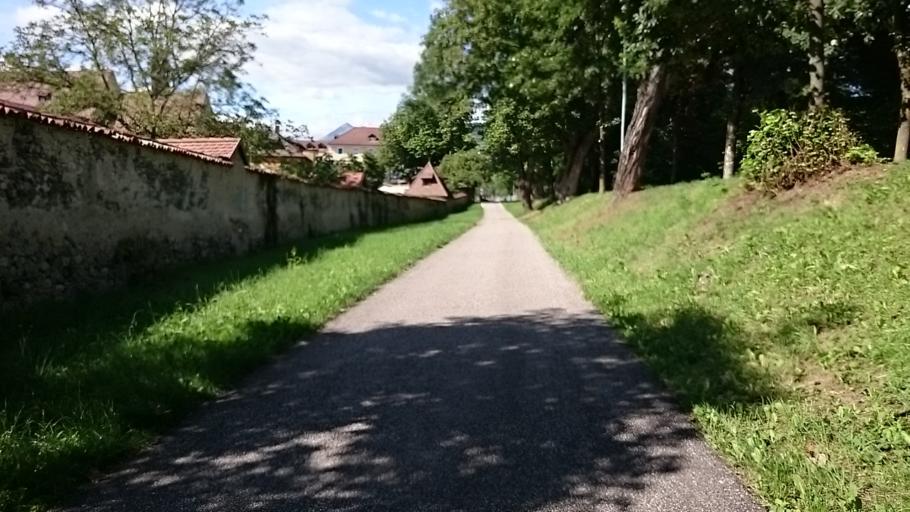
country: IT
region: Trentino-Alto Adige
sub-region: Bolzano
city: Bressanone
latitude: 46.7120
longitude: 11.6600
